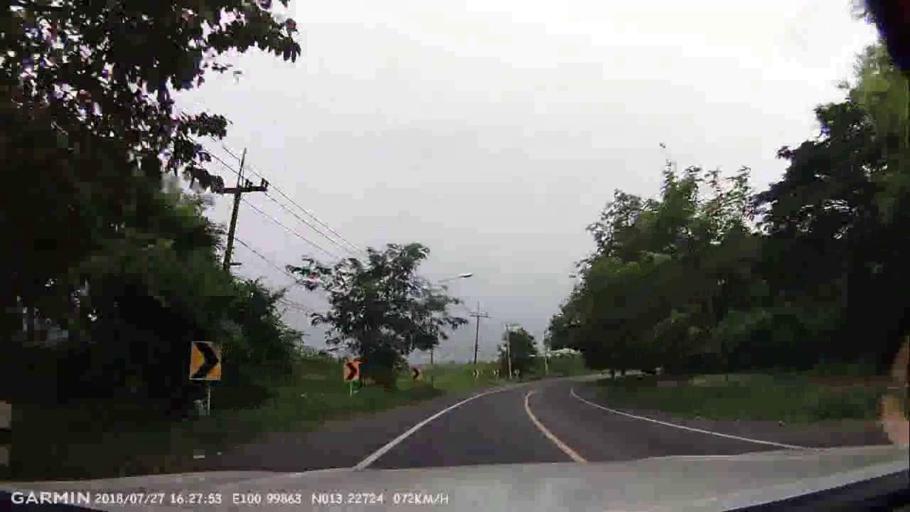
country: TH
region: Chon Buri
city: Si Racha
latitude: 13.2272
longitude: 100.9988
